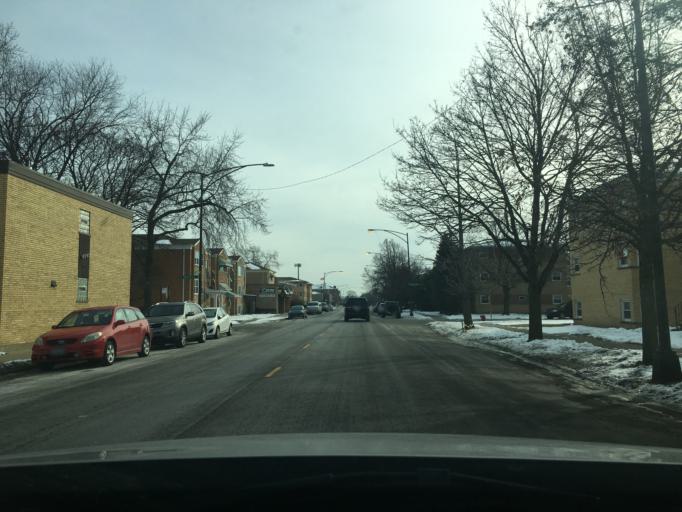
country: US
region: Illinois
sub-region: Cook County
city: Harwood Heights
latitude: 41.9776
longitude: -87.7920
